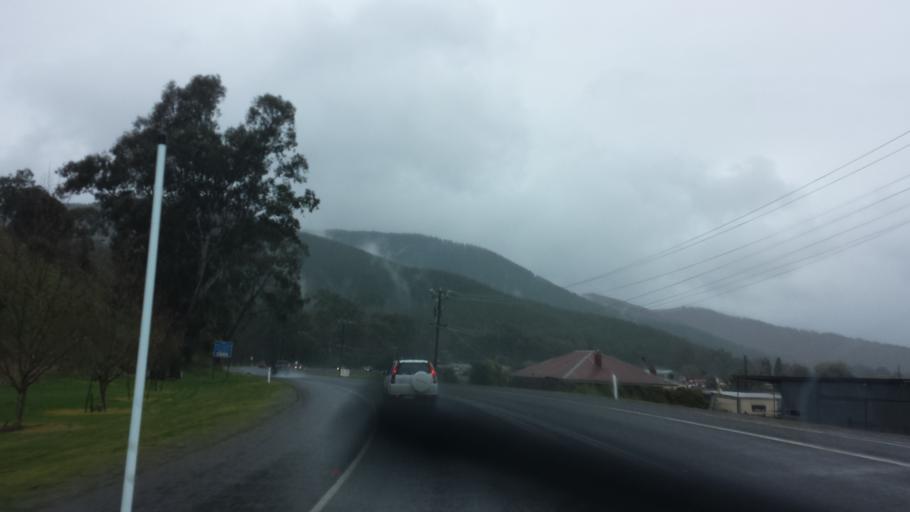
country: AU
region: Victoria
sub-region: Wangaratta
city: Wangaratta
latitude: -36.5703
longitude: 146.7326
